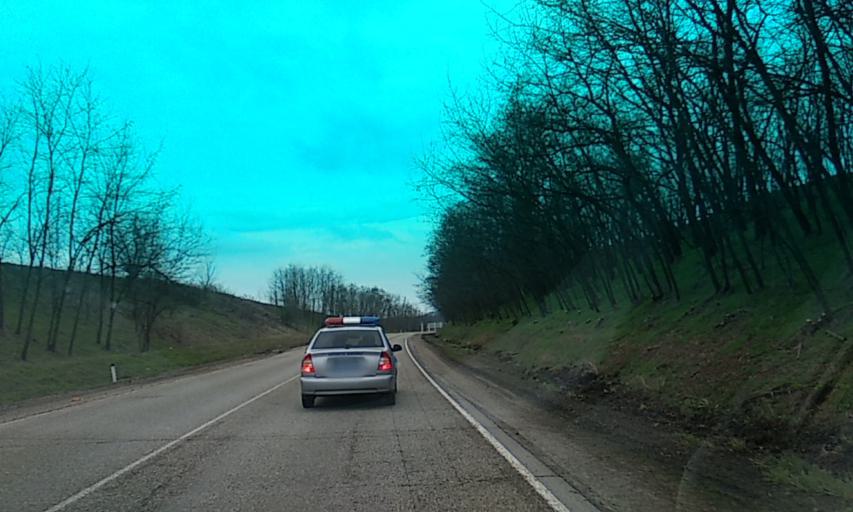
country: RU
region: Krasnodarskiy
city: Vyselki
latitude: 45.4458
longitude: 39.7086
